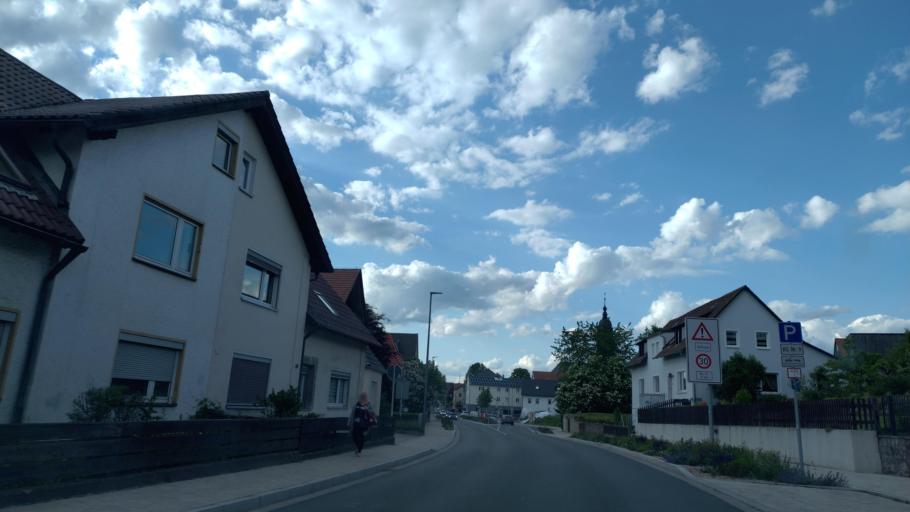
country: DE
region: Bavaria
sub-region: Upper Franconia
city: Bindlach
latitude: 49.9793
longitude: 11.6115
